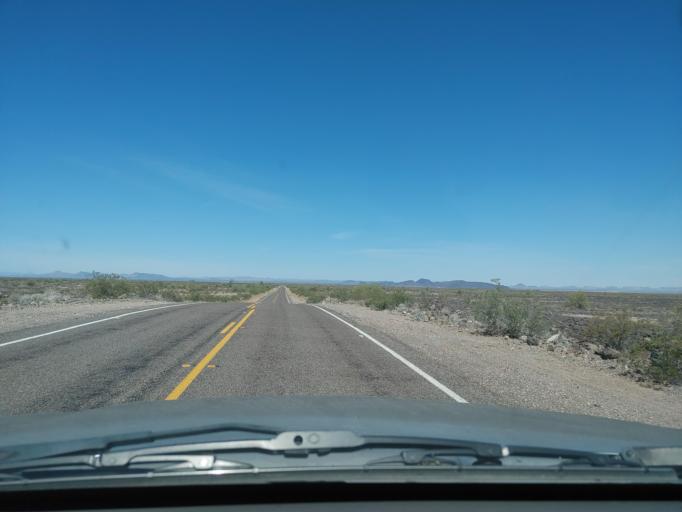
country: US
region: Arizona
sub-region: Maricopa County
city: Gila Bend
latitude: 32.9008
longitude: -113.2565
